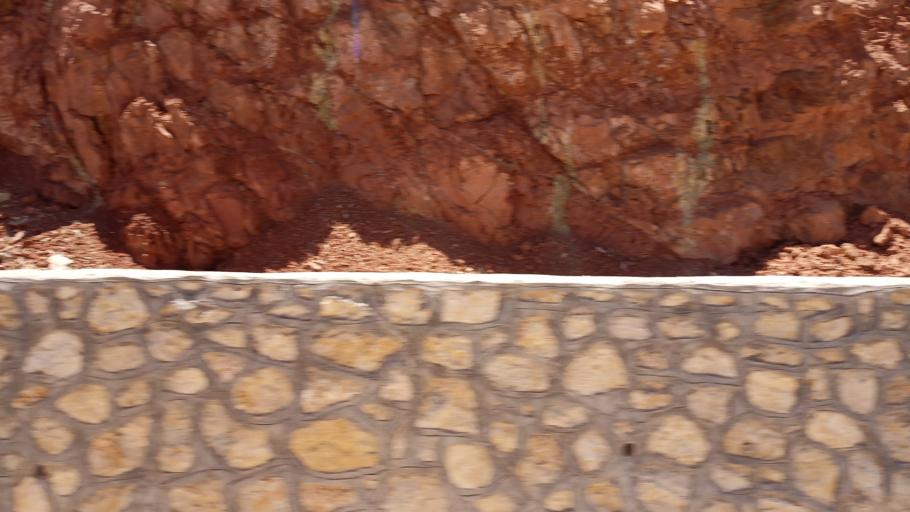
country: TR
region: Malatya
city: Darende
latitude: 38.6155
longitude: 37.4614
